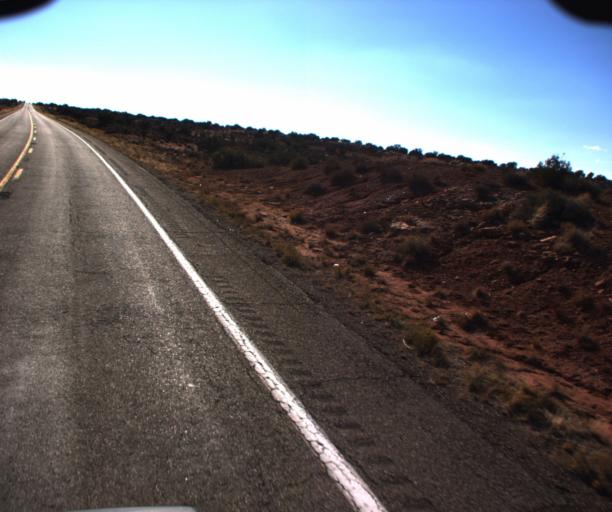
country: US
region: Arizona
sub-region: Coconino County
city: Kaibito
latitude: 36.6040
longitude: -111.0880
